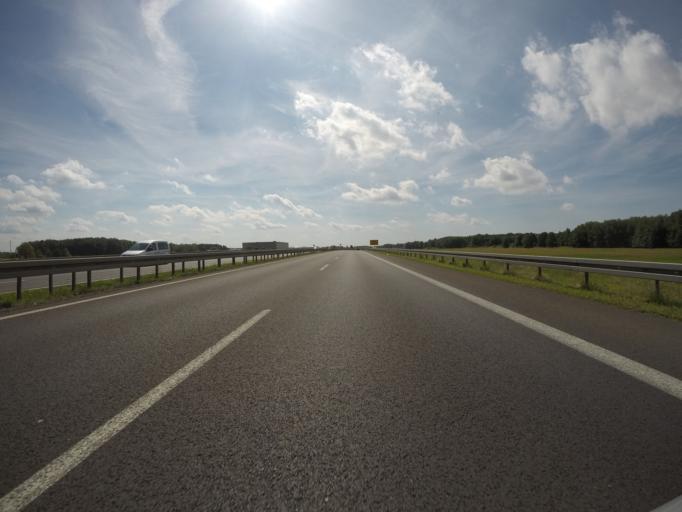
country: DE
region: Brandenburg
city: Leegebruch
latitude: 52.7266
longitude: 13.2155
